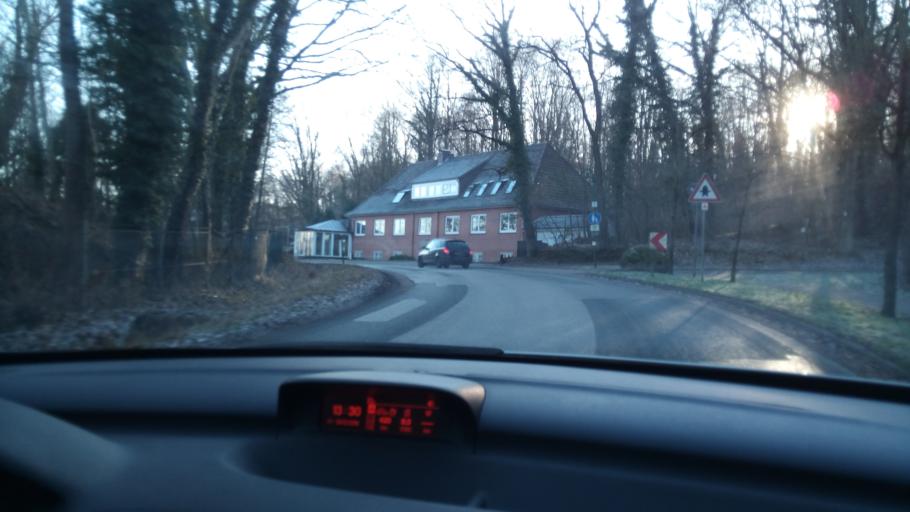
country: DE
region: Schleswig-Holstein
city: Buchhorst
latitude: 53.3822
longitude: 10.5708
